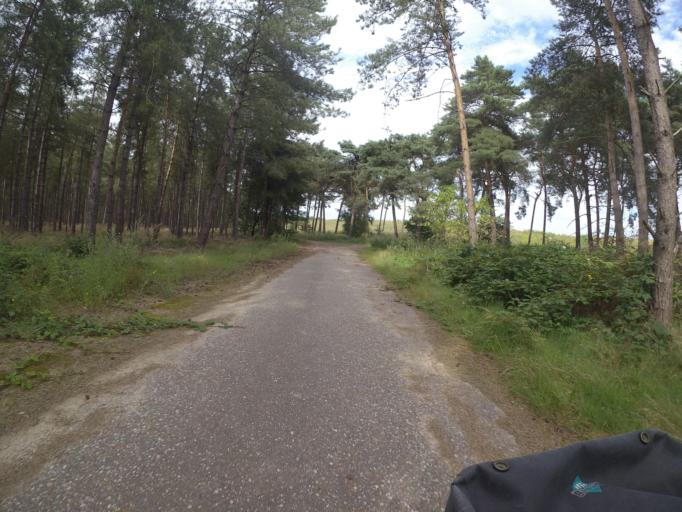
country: NL
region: North Brabant
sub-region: Gemeente Helmond
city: Helmond
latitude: 51.4319
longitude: 5.6824
